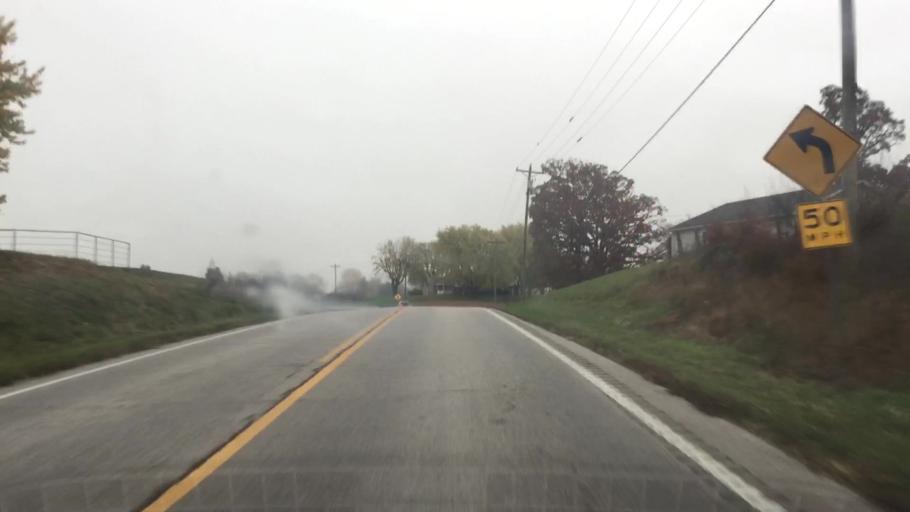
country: US
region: Missouri
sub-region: Callaway County
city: Fulton
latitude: 38.8585
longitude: -91.9968
